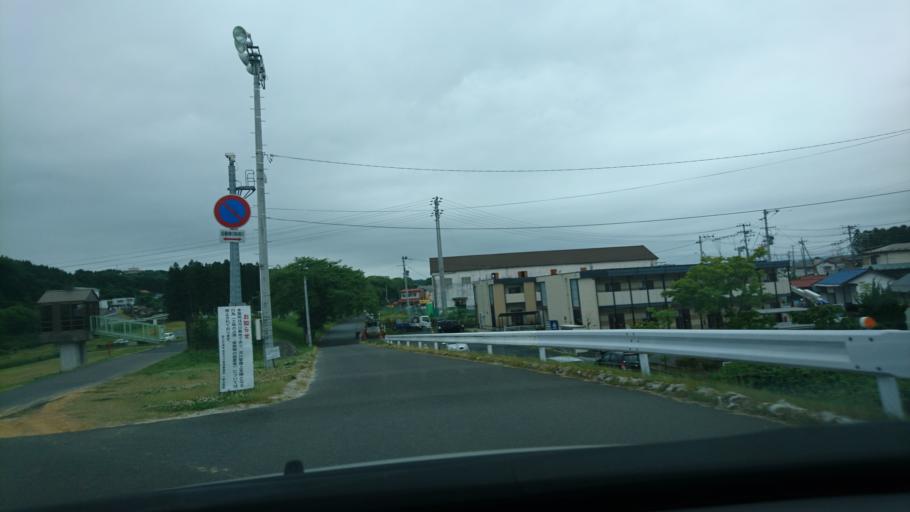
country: JP
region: Iwate
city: Ichinoseki
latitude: 38.9288
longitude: 141.1277
